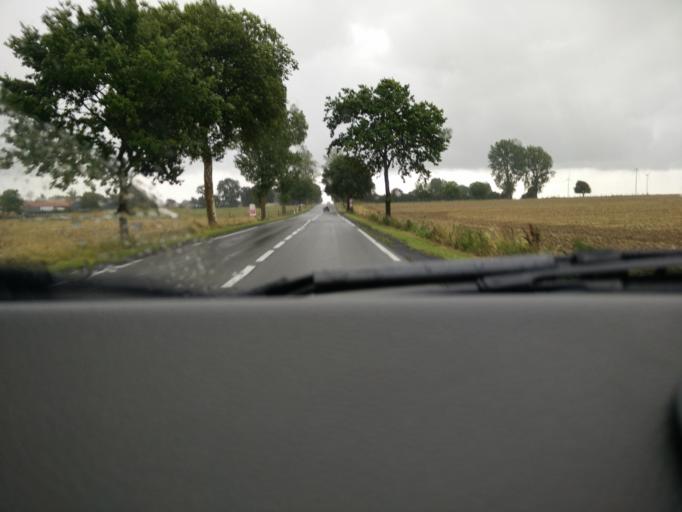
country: FR
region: Nord-Pas-de-Calais
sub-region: Departement du Pas-de-Calais
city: Savy-Berlette
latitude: 50.3572
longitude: 2.4726
